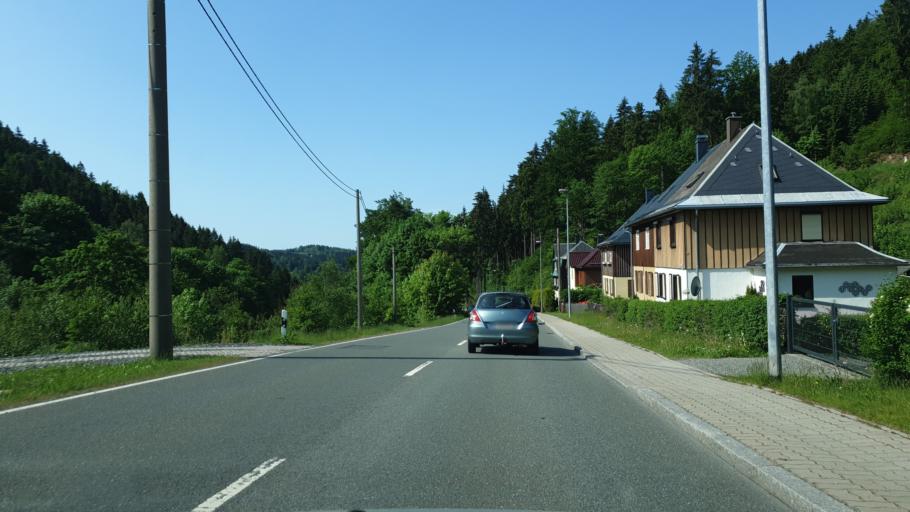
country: DE
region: Saxony
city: Klingenthal
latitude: 50.3907
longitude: 12.4945
